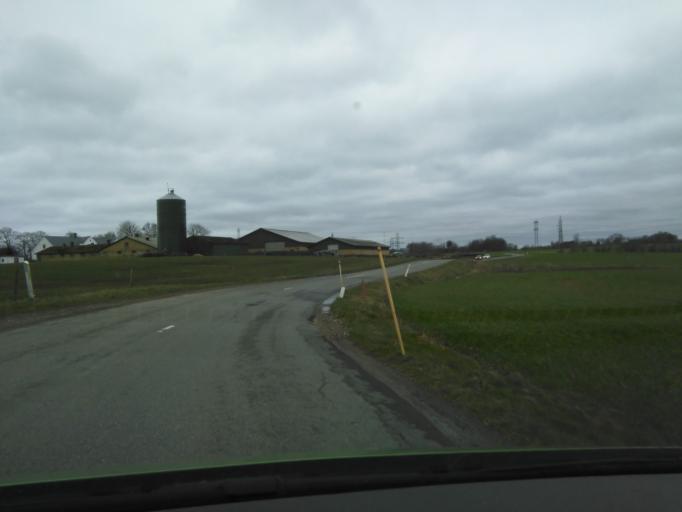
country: DK
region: Central Jutland
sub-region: Arhus Kommune
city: Marslet
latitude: 56.0474
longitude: 10.1486
